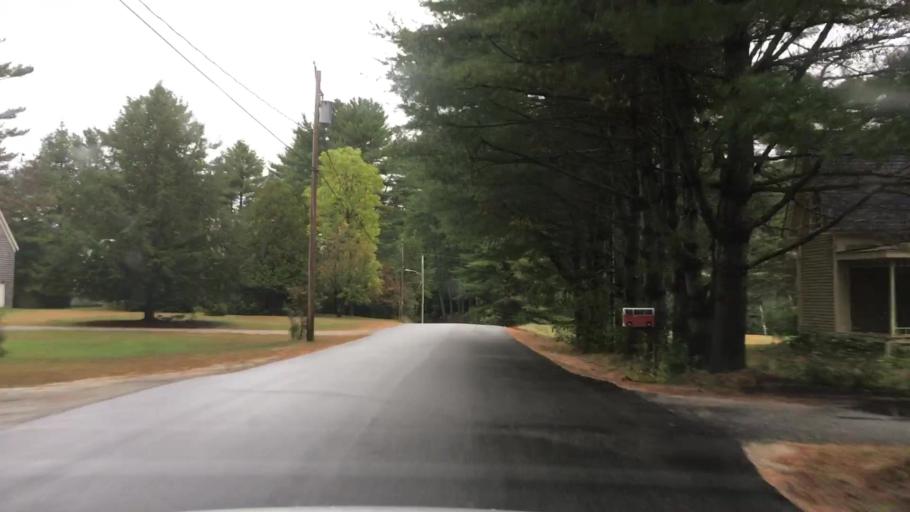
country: US
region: Maine
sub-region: Cumberland County
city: Raymond
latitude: 43.9981
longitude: -70.5686
